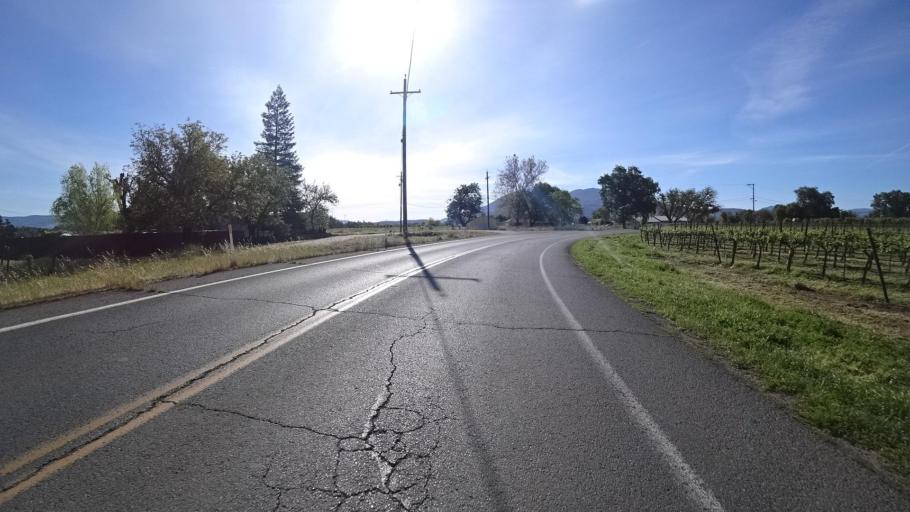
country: US
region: California
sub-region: Lake County
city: Kelseyville
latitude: 39.0149
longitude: -122.8578
